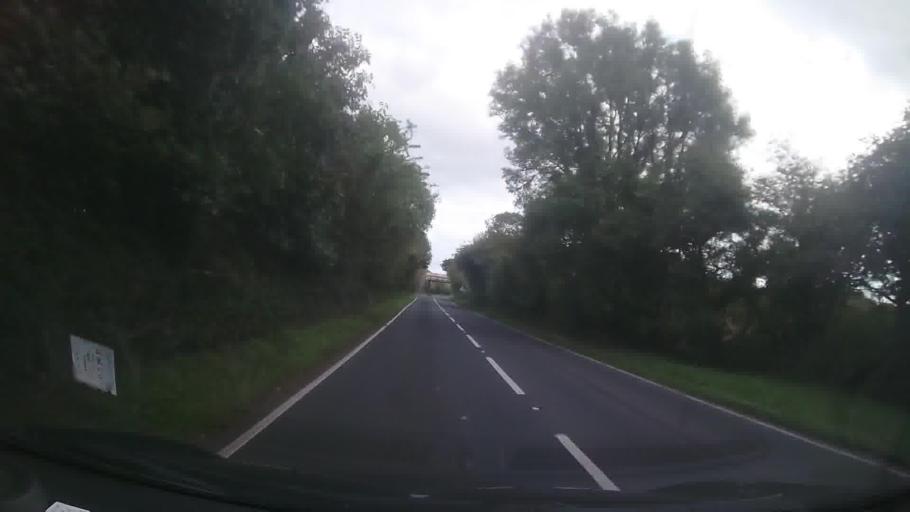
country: GB
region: Wales
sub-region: Pembrokeshire
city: Kilgetty
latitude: 51.7103
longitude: -4.7295
